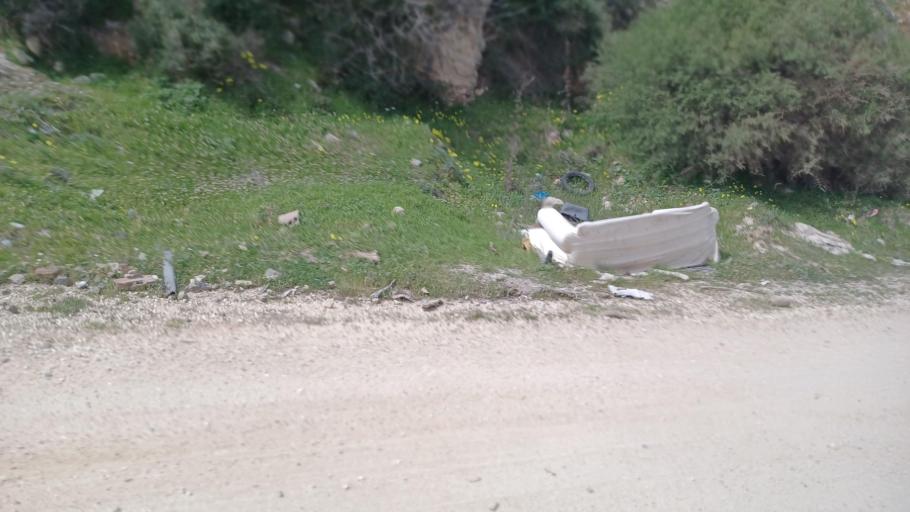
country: CY
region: Pafos
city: Polis
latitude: 35.0002
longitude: 32.3965
